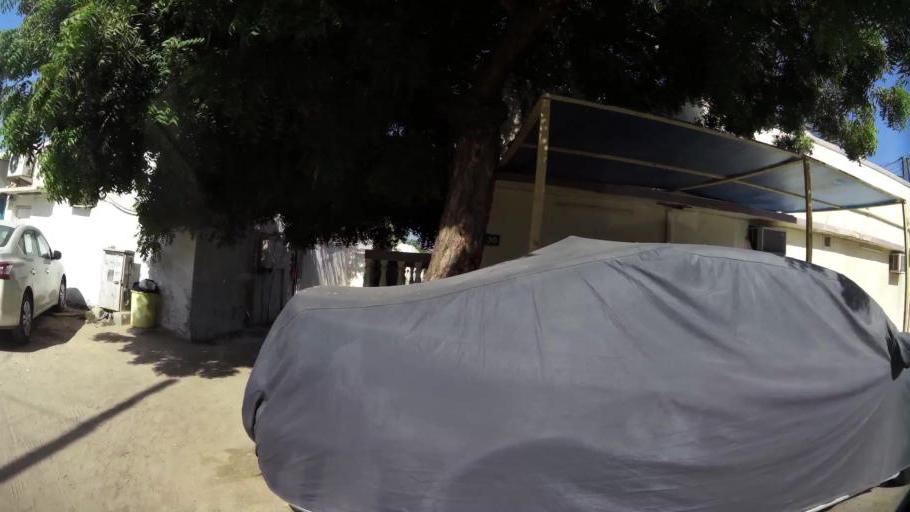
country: AE
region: Ajman
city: Ajman
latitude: 25.4141
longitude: 55.4515
